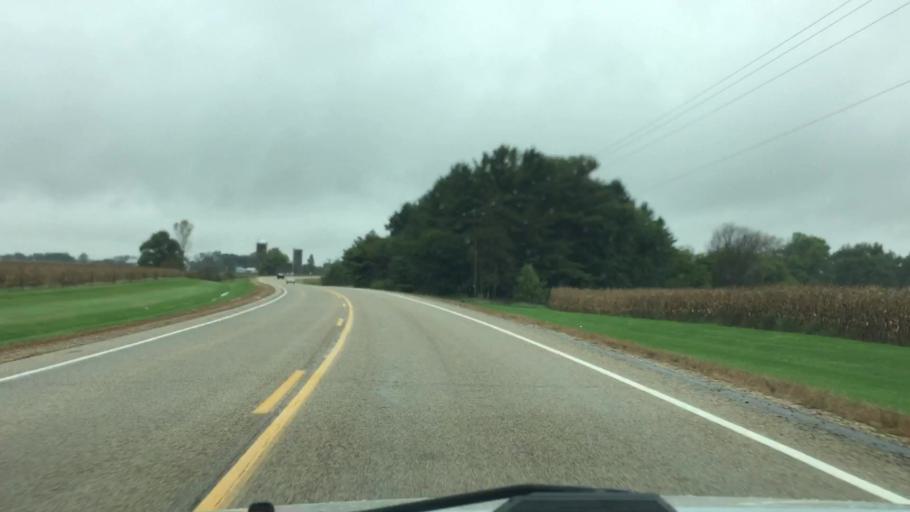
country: US
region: Wisconsin
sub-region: Jefferson County
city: Palmyra
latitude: 42.8755
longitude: -88.6373
